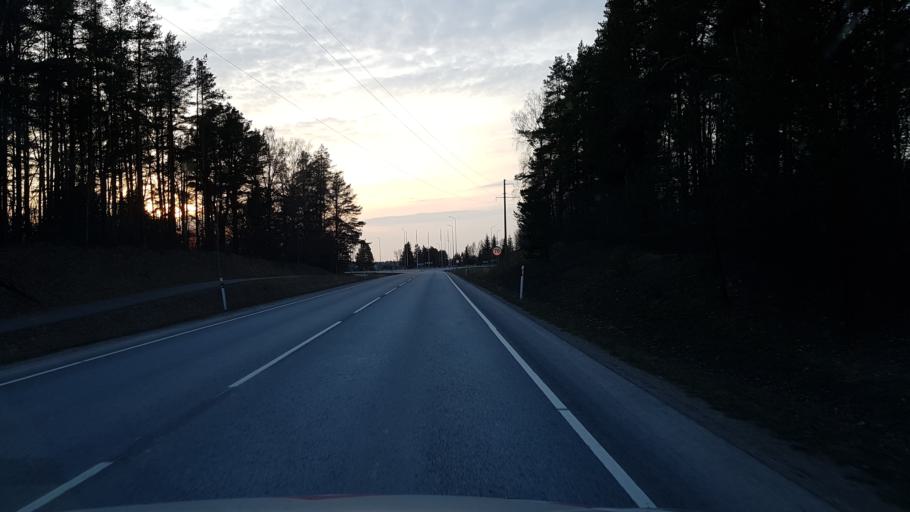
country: EE
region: Laeaene-Virumaa
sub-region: Rakvere linn
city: Rakvere
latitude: 59.3248
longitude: 26.3529
